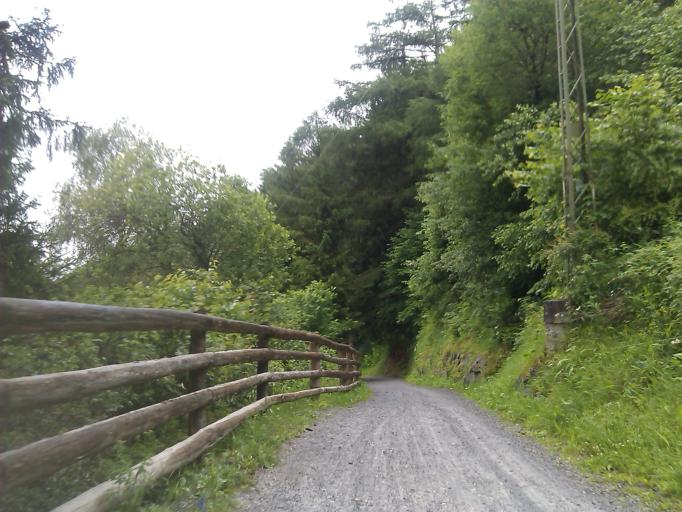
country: IT
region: Trentino-Alto Adige
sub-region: Bolzano
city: Lasa
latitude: 46.6101
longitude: 10.7180
